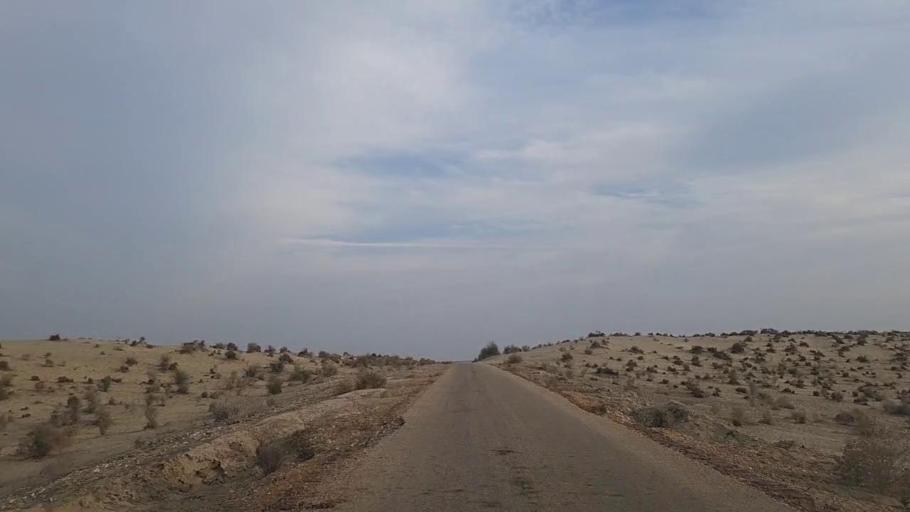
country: PK
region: Sindh
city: Daur
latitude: 26.5089
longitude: 68.5104
